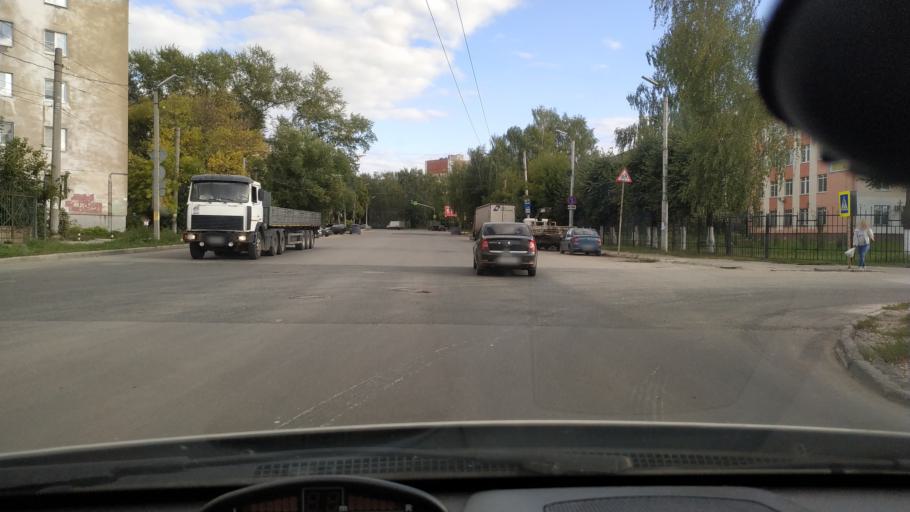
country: RU
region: Rjazan
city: Ryazan'
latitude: 54.6071
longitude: 39.7031
